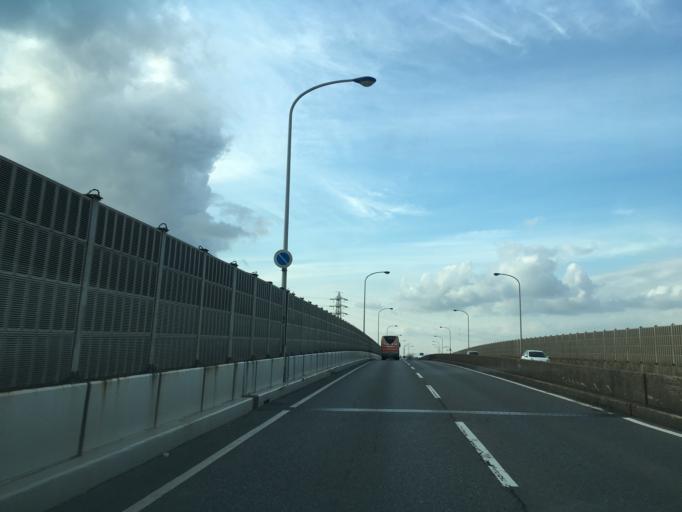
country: JP
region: Chiba
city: Kisarazu
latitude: 35.3856
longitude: 139.9417
